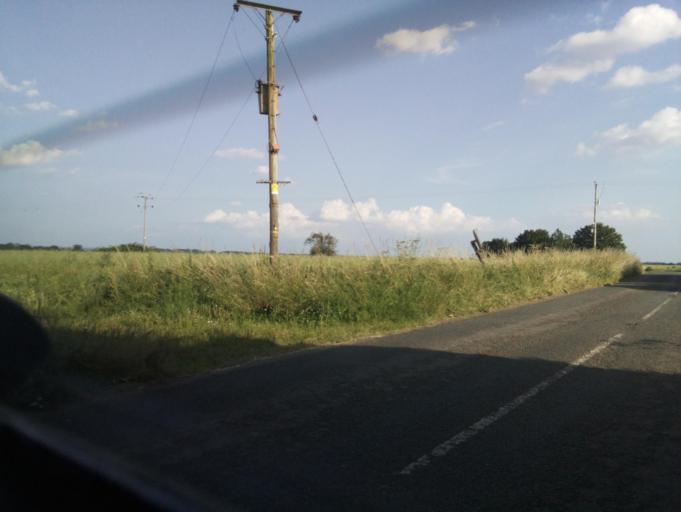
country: GB
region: England
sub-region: South Gloucestershire
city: Marshfield
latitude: 51.4786
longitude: -2.3117
